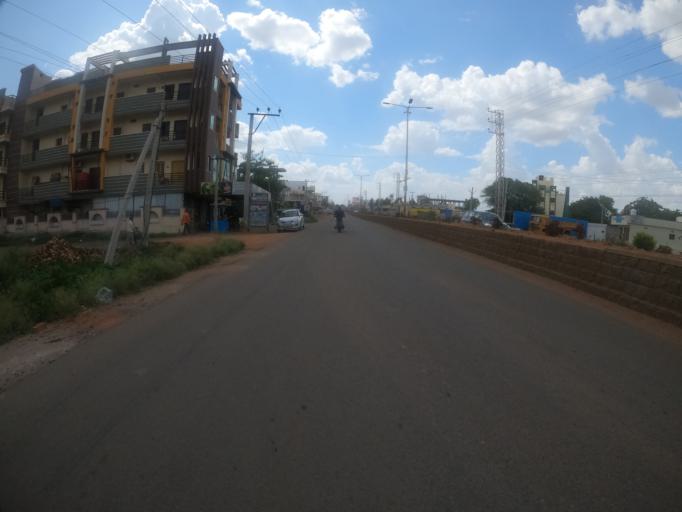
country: IN
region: Telangana
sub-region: Rangareddi
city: Sriramnagar
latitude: 17.3079
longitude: 78.1435
